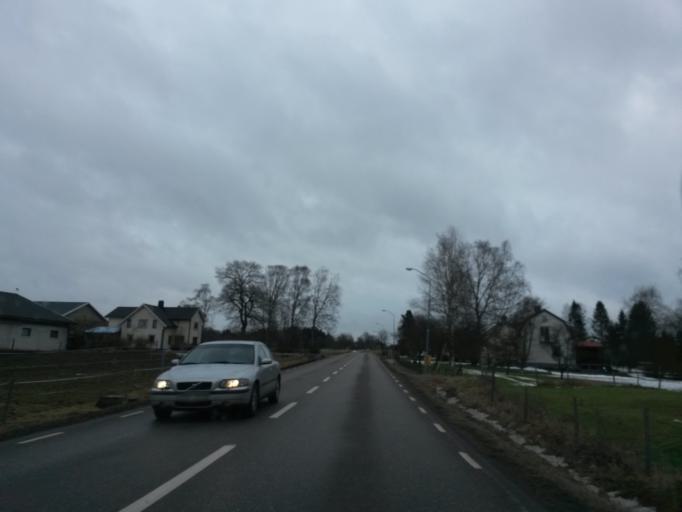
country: SE
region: Vaestra Goetaland
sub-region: Herrljunga Kommun
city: Herrljunga
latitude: 58.0617
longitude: 12.9373
